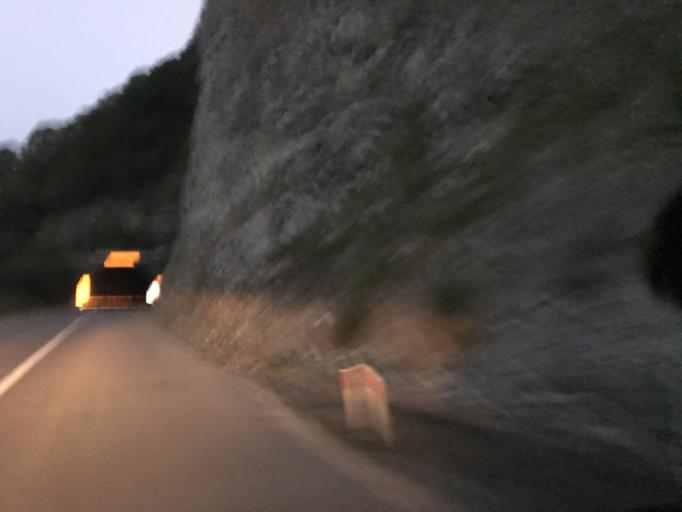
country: RO
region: Caras-Severin
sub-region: Comuna Berzasca
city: Berzasca
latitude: 44.6169
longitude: 21.9969
